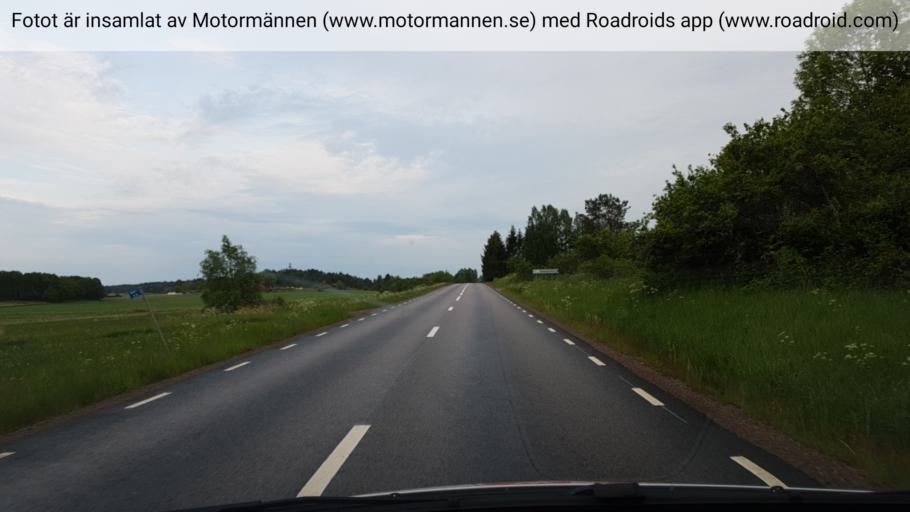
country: SE
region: Kalmar
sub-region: Vasterviks Kommun
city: Forserum
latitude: 57.9452
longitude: 16.4494
